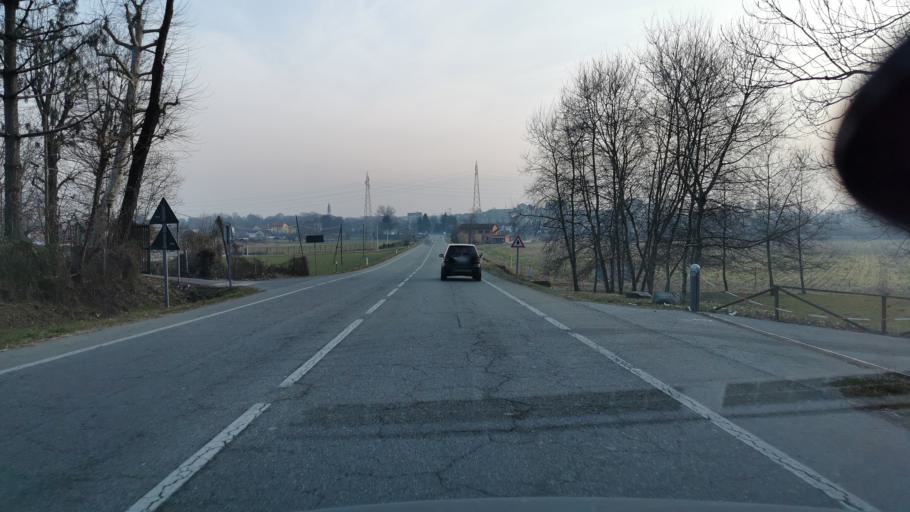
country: IT
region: Piedmont
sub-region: Provincia di Torino
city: Venaria Reale
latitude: 45.1450
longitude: 7.6252
